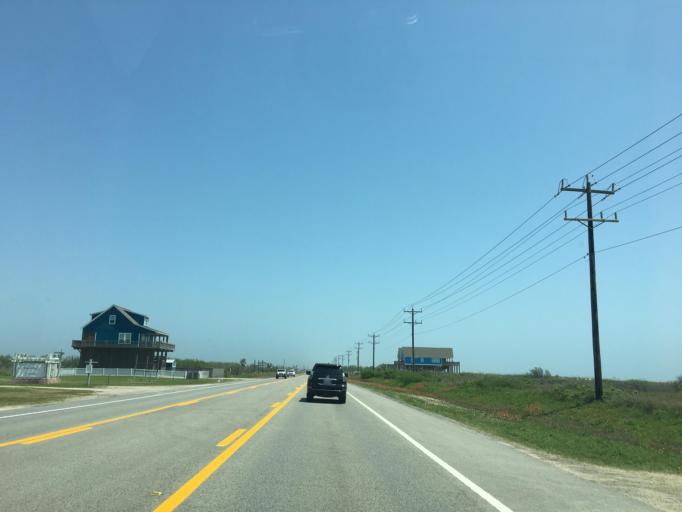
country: US
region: Texas
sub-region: Galveston County
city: Bolivar Peninsula
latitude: 29.5061
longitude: -94.5064
